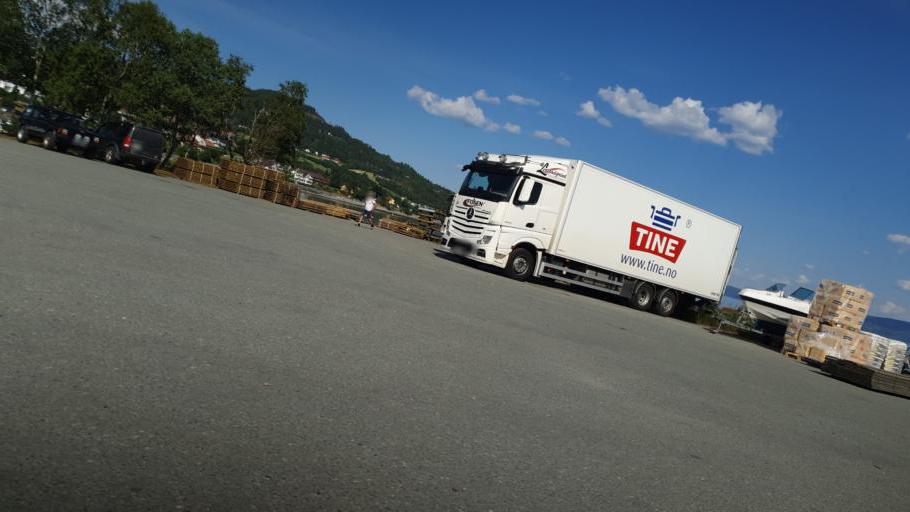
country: NO
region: Nord-Trondelag
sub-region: Leksvik
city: Leksvik
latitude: 63.6682
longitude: 10.6182
